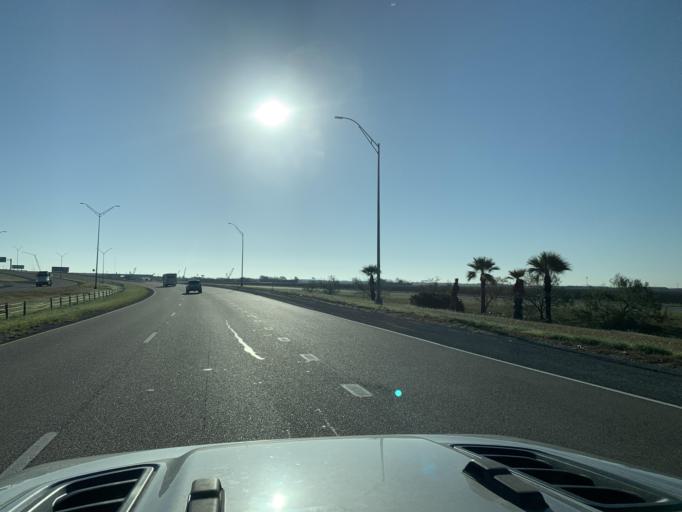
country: US
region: Texas
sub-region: Nueces County
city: Corpus Christi
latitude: 27.7827
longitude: -97.4831
